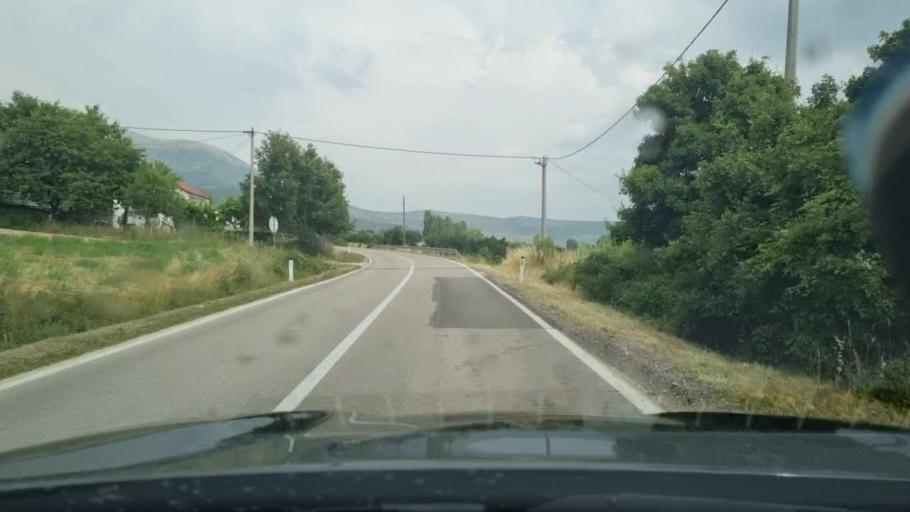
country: BA
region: Federation of Bosnia and Herzegovina
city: Podhum
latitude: 43.6878
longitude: 17.0668
